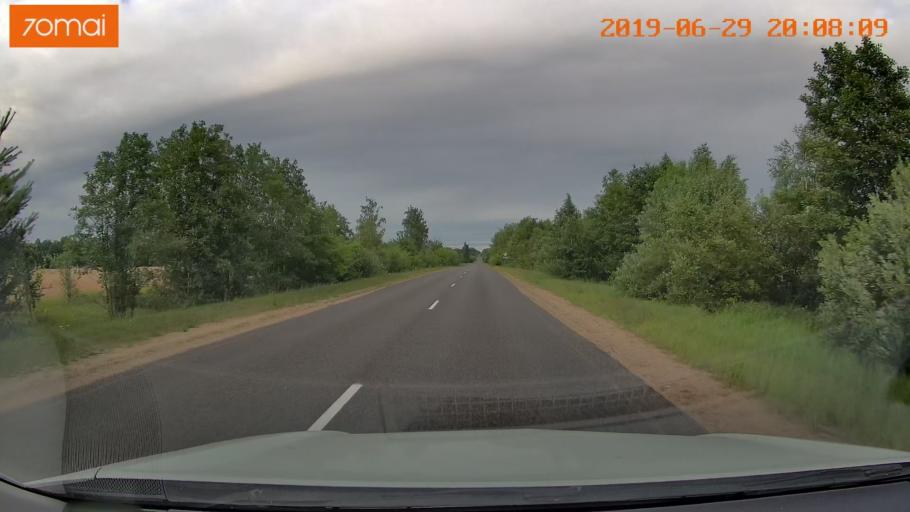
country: BY
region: Brest
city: Lahishyn
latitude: 52.3435
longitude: 26.0521
